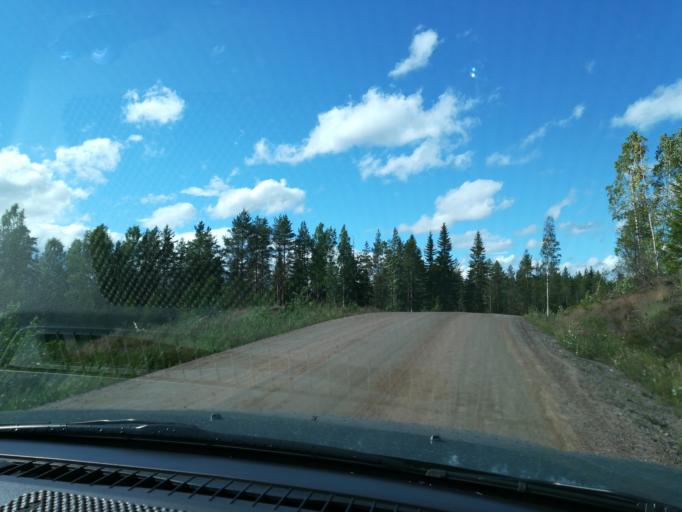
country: FI
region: South Karelia
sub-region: Lappeenranta
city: Savitaipale
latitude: 61.2992
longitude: 27.6397
